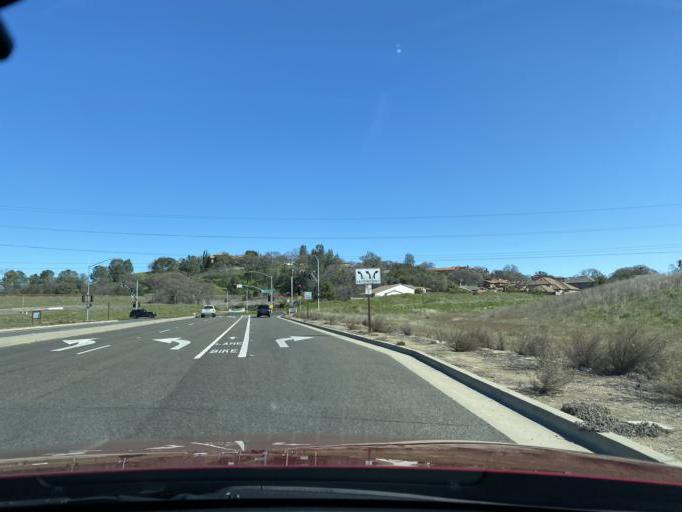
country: US
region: California
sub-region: Sacramento County
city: Folsom
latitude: 38.6931
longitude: -121.1440
